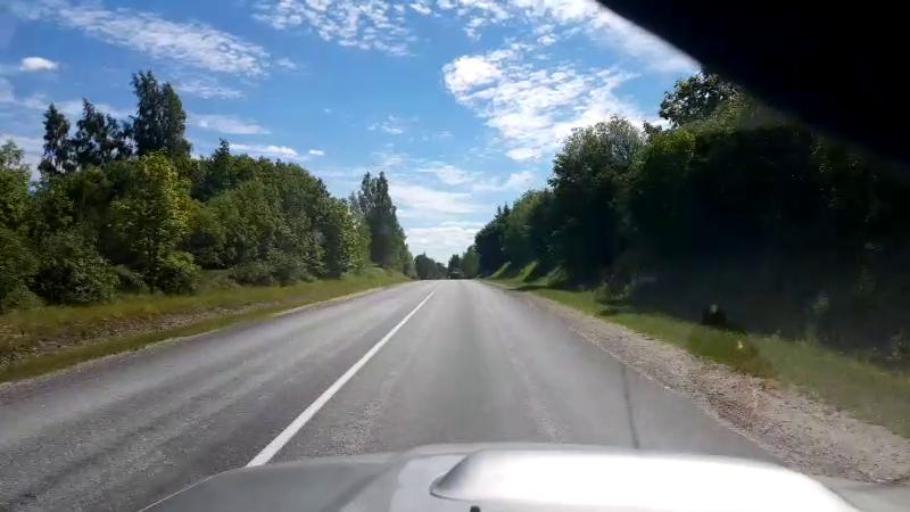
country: EE
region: Laeaene-Virumaa
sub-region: Rakke vald
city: Rakke
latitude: 58.8482
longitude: 26.2911
